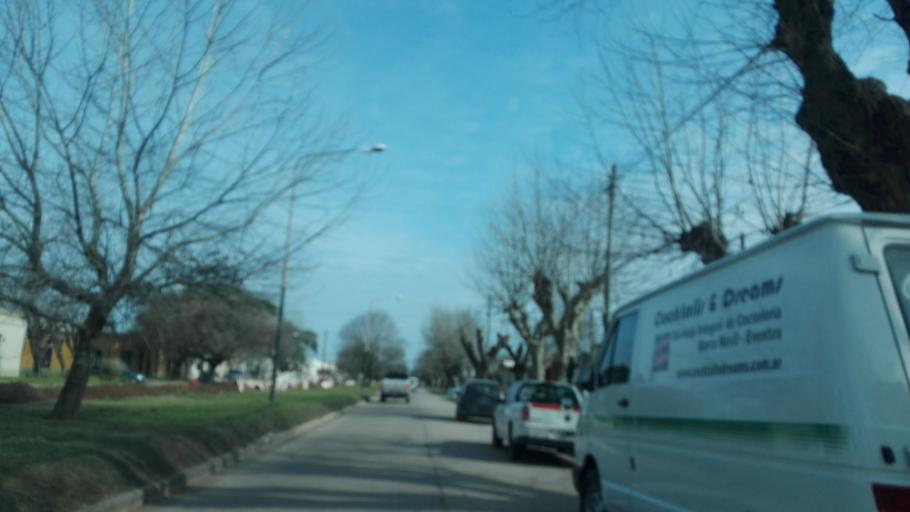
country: AR
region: Buenos Aires
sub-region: Partido de Chascomus
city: Chascomus
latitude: -35.5677
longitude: -58.0120
